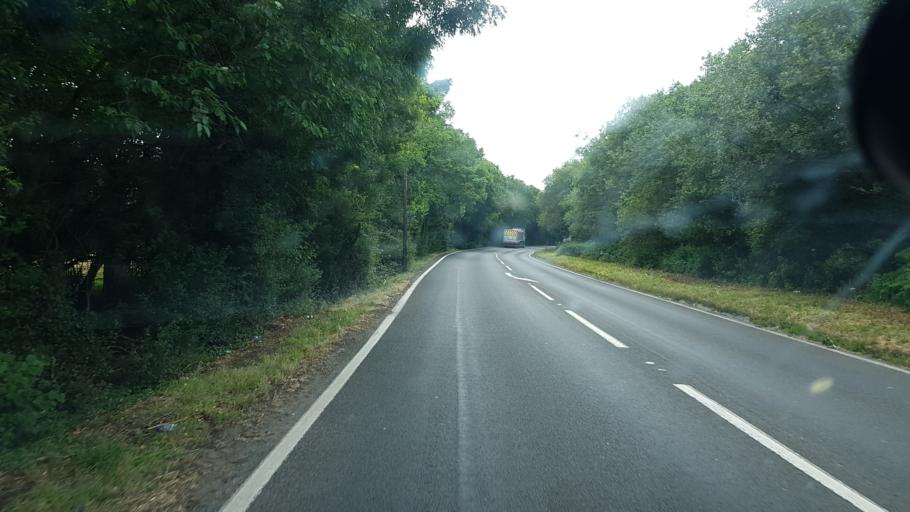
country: GB
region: England
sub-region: Surrey
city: Felbridge
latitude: 51.1691
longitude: -0.0503
